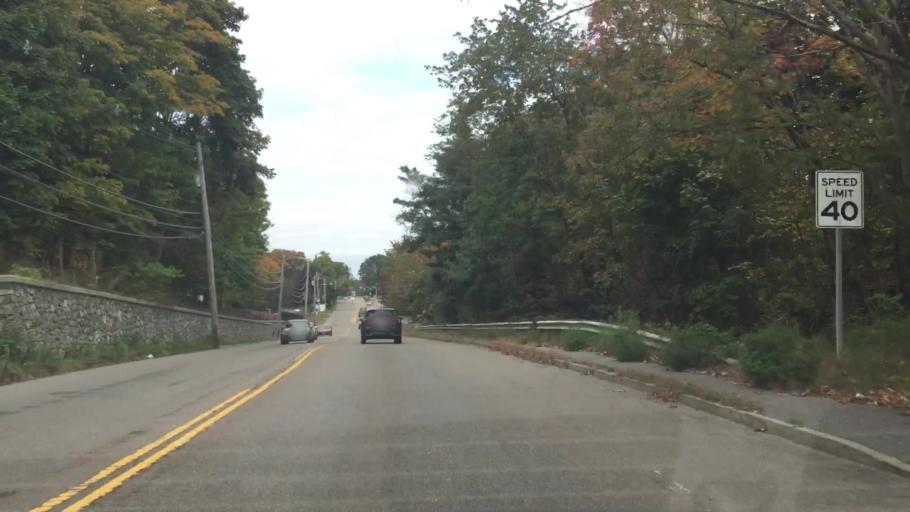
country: US
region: Massachusetts
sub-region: Essex County
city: Middleton
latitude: 42.5970
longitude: -71.0179
